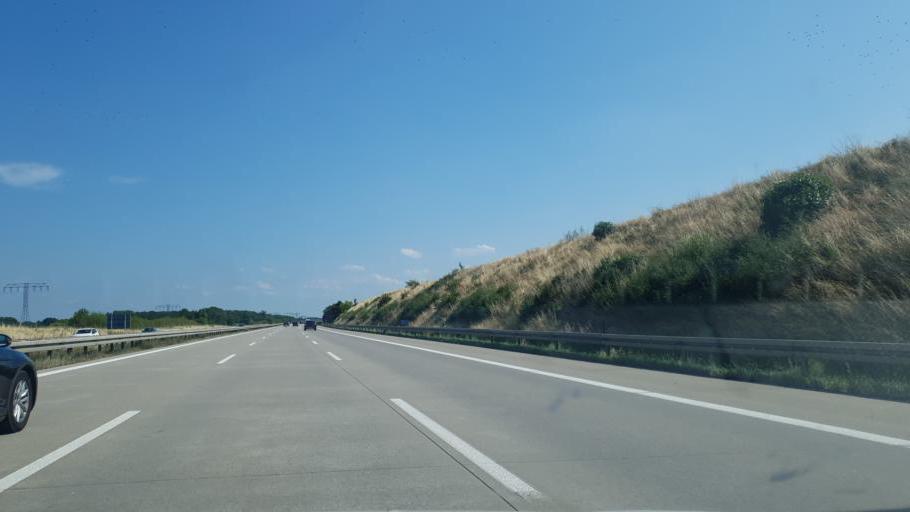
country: DE
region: Brandenburg
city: Neuenhagen
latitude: 52.5320
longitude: 13.7064
